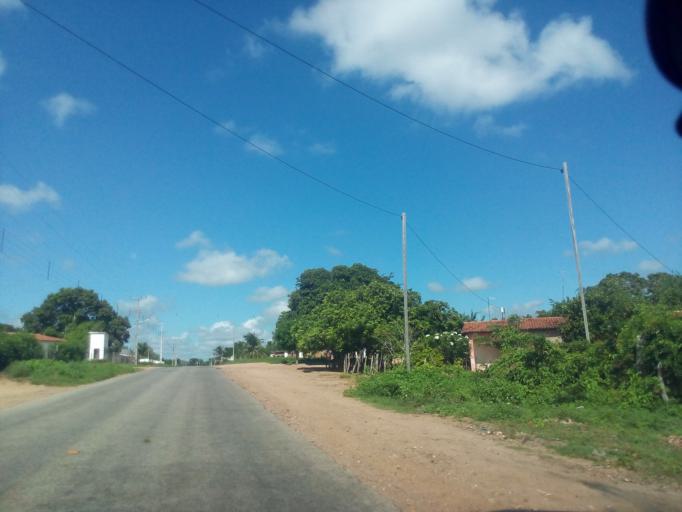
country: BR
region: Rio Grande do Norte
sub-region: Sao Paulo Do Potengi
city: Sao Paulo do Potengi
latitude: -5.9131
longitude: -35.7043
